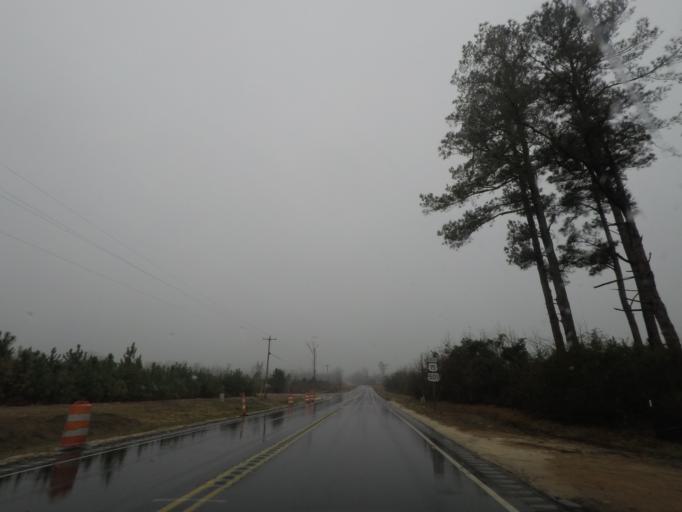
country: US
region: North Carolina
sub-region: Scotland County
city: Laurinburg
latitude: 34.8398
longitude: -79.4591
